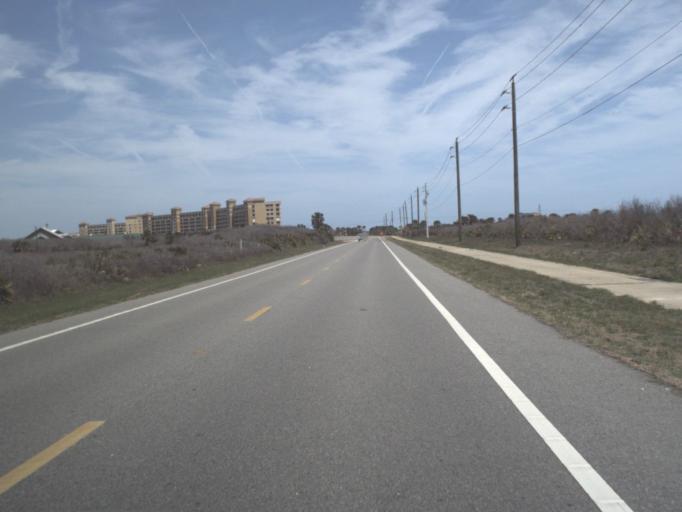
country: US
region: Florida
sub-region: Flagler County
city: Palm Coast
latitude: 29.6397
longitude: -81.2038
